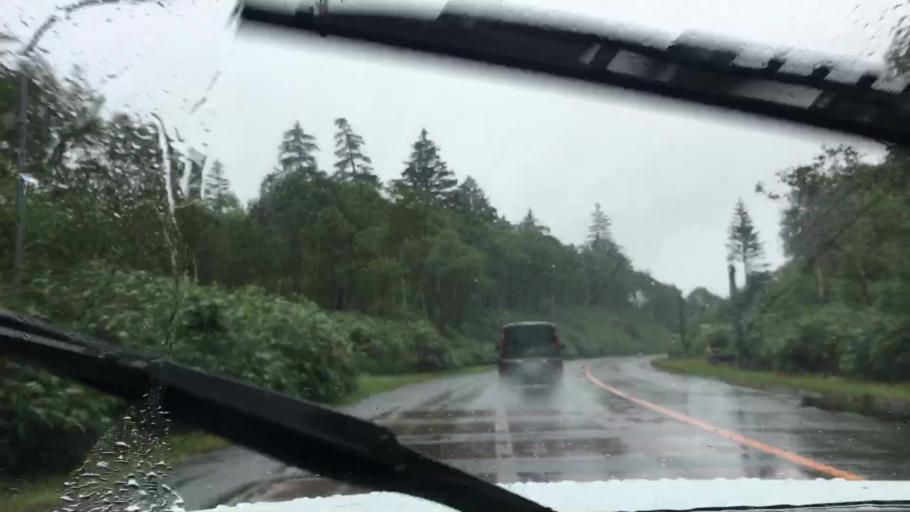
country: JP
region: Hokkaido
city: Sapporo
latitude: 42.8659
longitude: 141.1099
